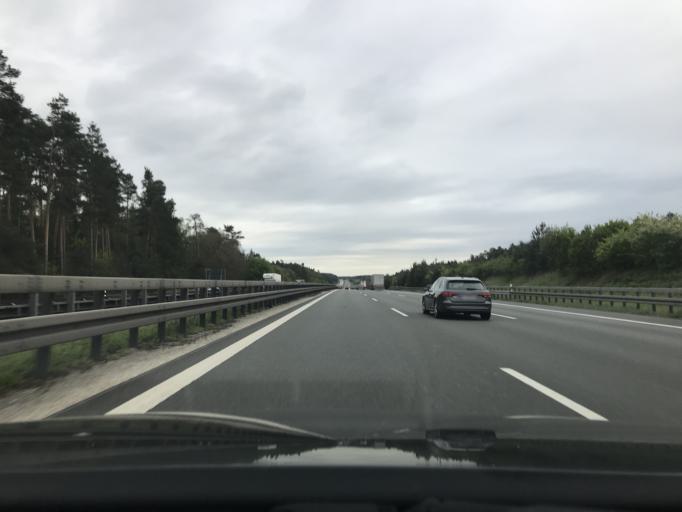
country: DE
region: Bavaria
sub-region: Regierungsbezirk Mittelfranken
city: Allersberg
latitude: 49.3020
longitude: 11.2077
